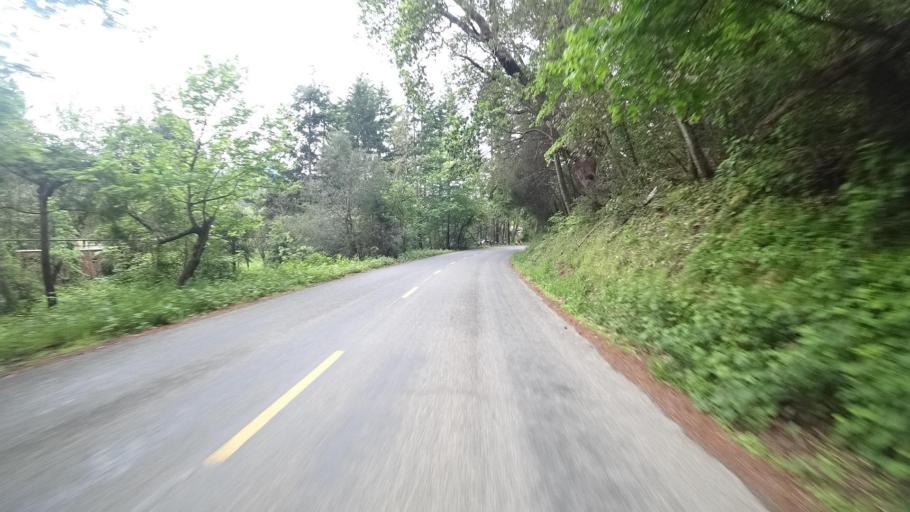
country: US
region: California
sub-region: Humboldt County
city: Willow Creek
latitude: 40.9567
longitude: -123.6294
